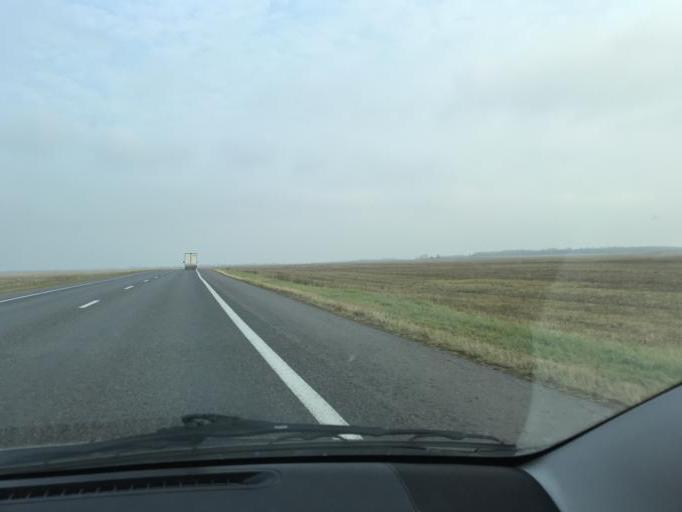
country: BY
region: Vitebsk
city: Syanno
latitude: 55.0940
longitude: 29.6418
